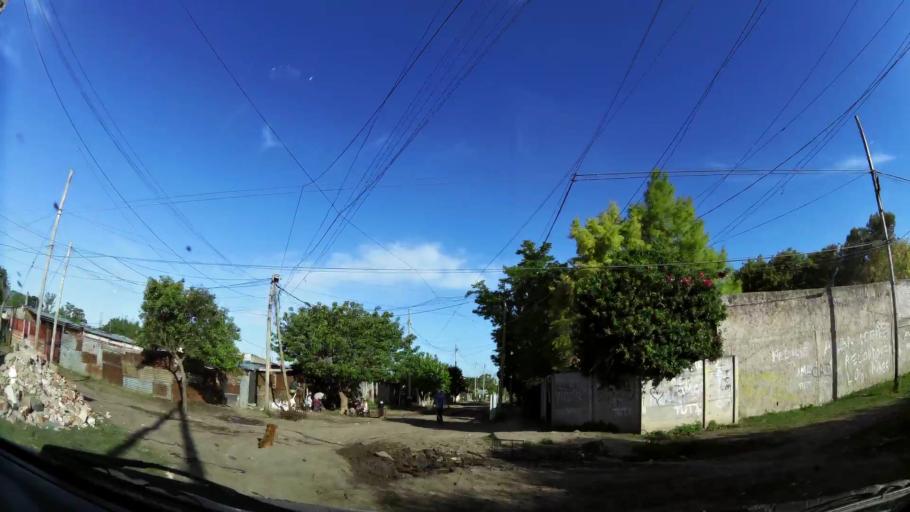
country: AR
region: Buenos Aires
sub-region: Partido de Quilmes
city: Quilmes
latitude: -34.8212
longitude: -58.2138
